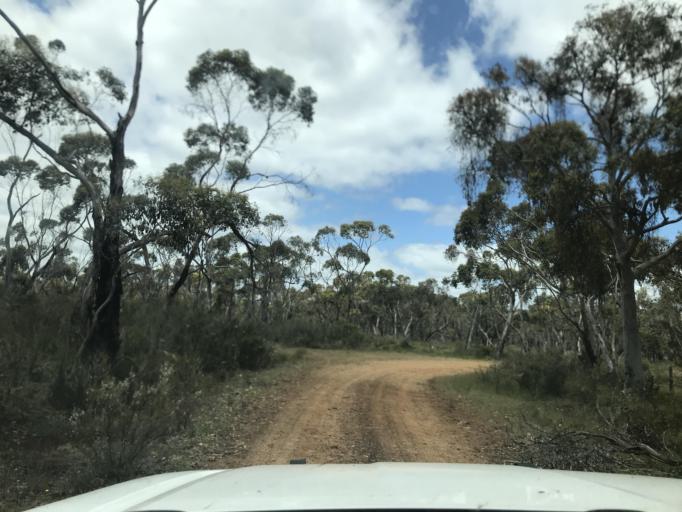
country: AU
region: South Australia
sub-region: Wattle Range
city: Penola
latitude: -37.3619
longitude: 141.1137
